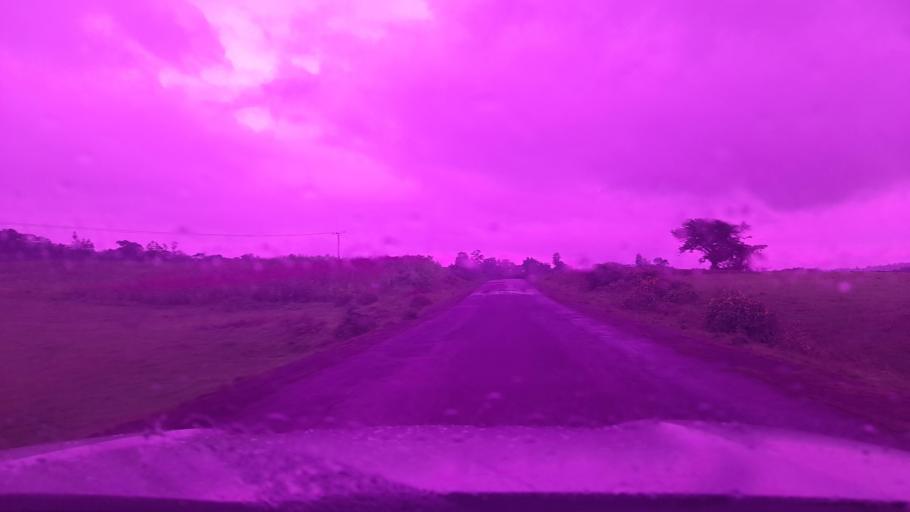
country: ET
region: Oromiya
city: Jima
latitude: 7.7732
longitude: 37.3414
